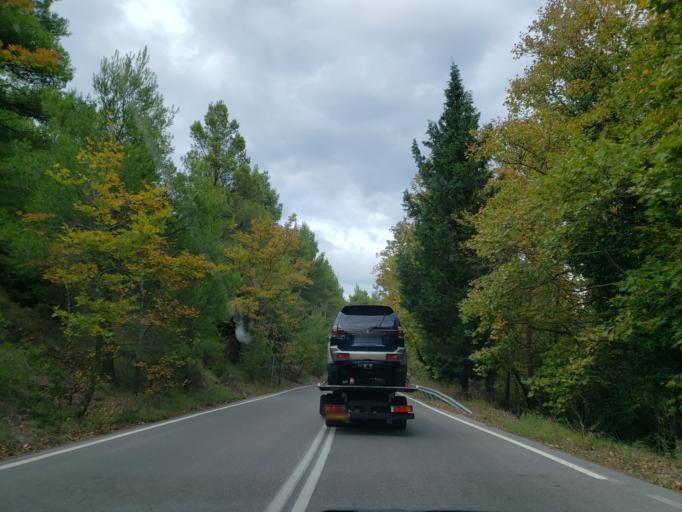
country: GR
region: Attica
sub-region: Nomarchia Anatolikis Attikis
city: Varnavas
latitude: 38.2159
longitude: 23.9137
